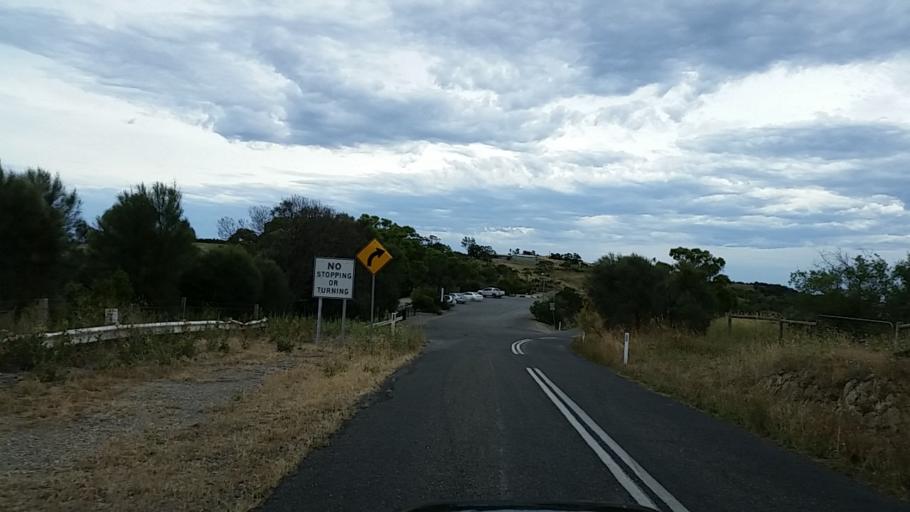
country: AU
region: South Australia
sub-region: Yankalilla
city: Normanville
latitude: -35.3992
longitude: 138.4188
